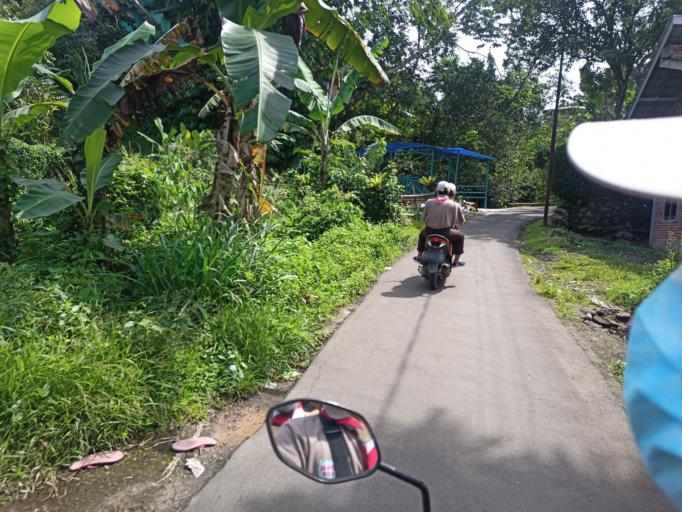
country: ID
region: West Java
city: Caringin
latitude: -6.6434
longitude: 106.9089
